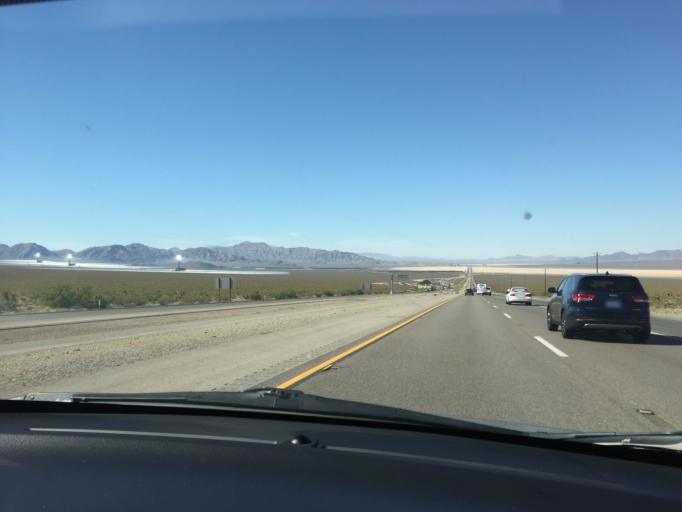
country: US
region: Nevada
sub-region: Clark County
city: Sandy Valley
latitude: 35.4867
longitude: -115.4427
